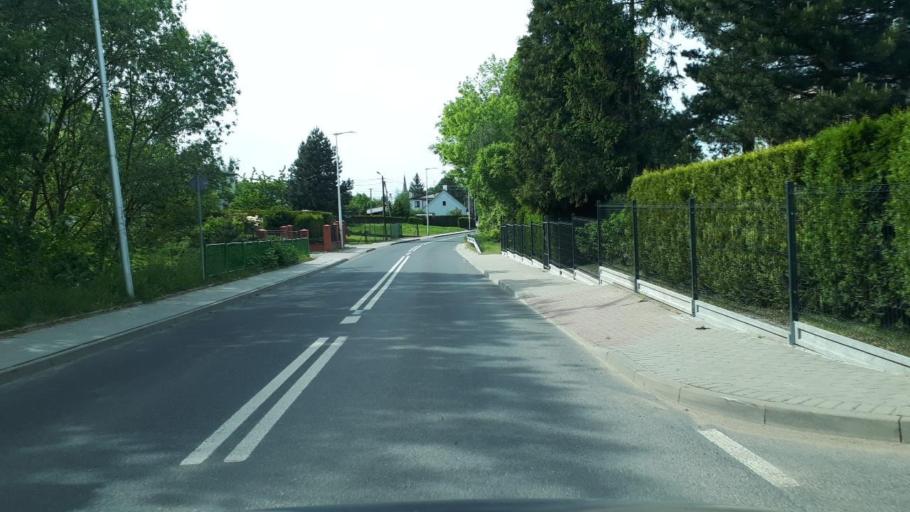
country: PL
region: Silesian Voivodeship
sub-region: Powiat bielski
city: Kozy
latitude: 49.8421
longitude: 19.1453
